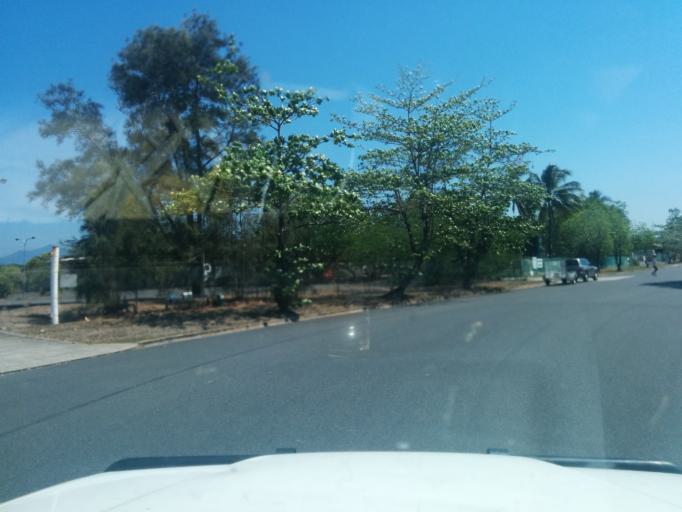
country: AU
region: Queensland
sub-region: Cairns
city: Cairns
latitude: -16.9432
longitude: 145.7732
